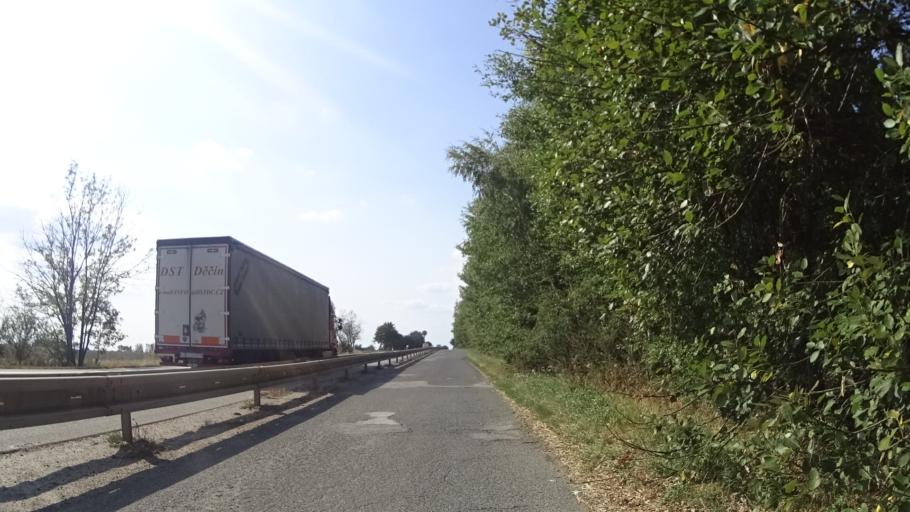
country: CZ
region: Kralovehradecky
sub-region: Okres Jicin
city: Sobotka
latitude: 50.4603
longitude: 15.2101
